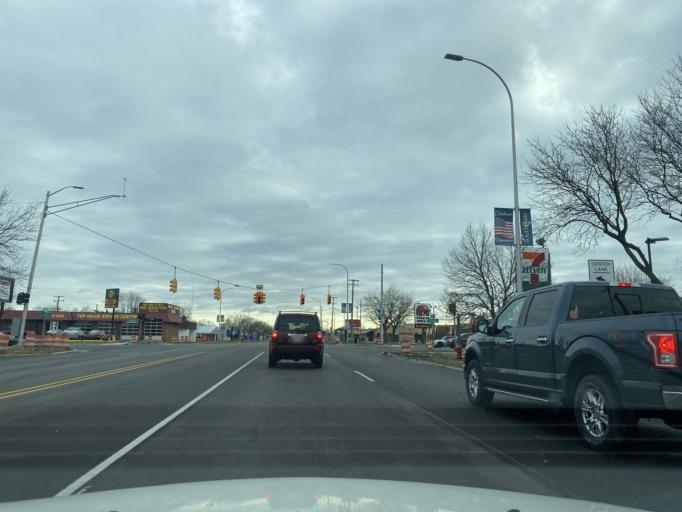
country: US
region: Michigan
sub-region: Wayne County
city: Southgate
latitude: 42.1992
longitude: -83.1937
